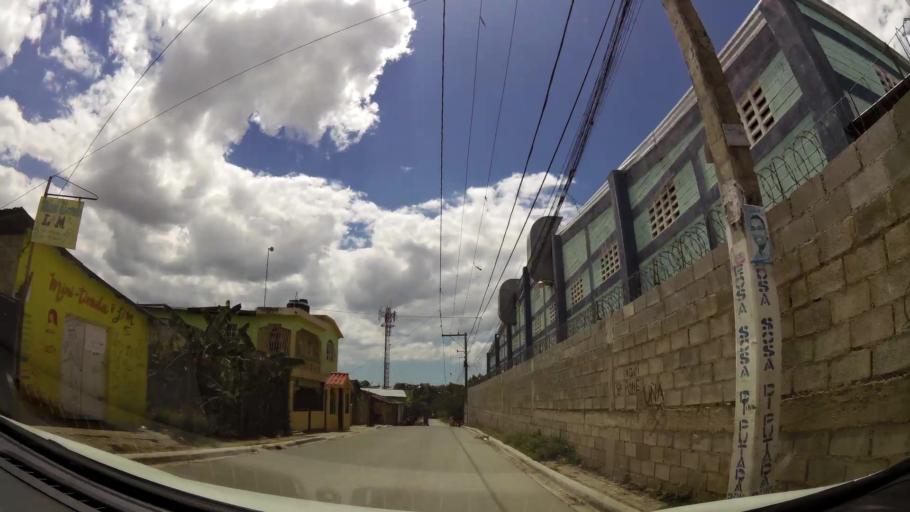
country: DO
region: Nacional
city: Ensanche Luperon
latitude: 18.5151
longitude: -69.9043
